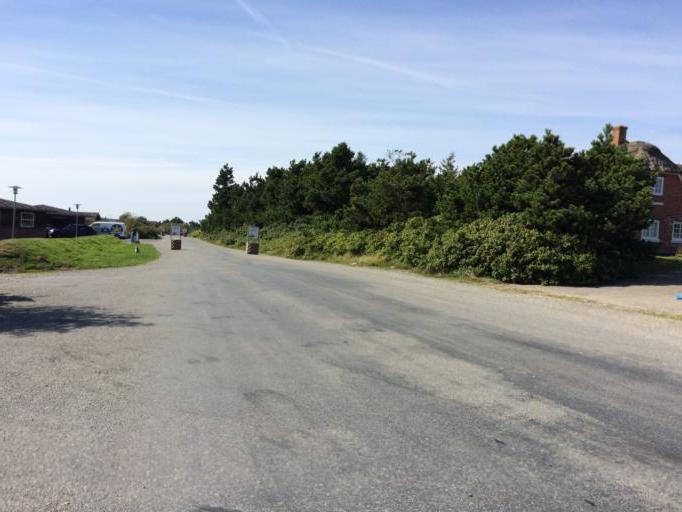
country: DK
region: Central Jutland
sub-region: Ringkobing-Skjern Kommune
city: Hvide Sande
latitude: 55.8642
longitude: 8.1808
